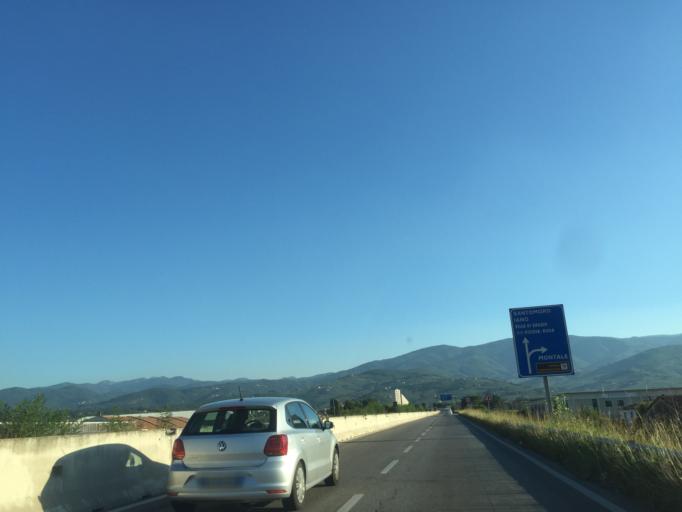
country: IT
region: Tuscany
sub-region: Provincia di Pistoia
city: Pistoia
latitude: 43.9326
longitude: 10.9336
